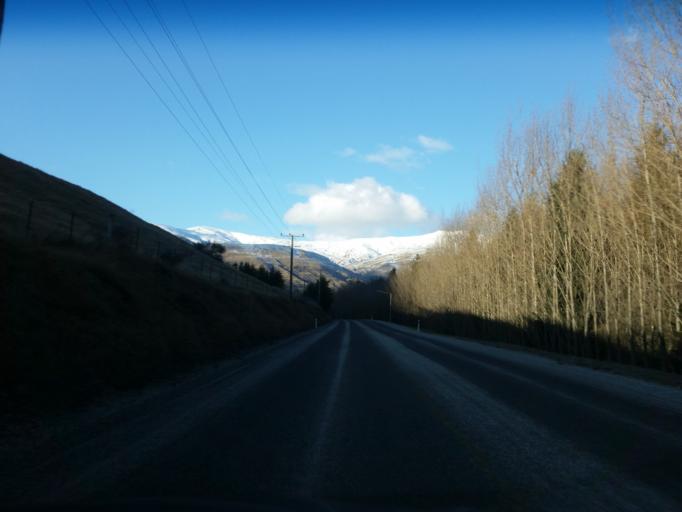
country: NZ
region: Otago
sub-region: Queenstown-Lakes District
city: Arrowtown
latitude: -44.9459
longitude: 168.7945
